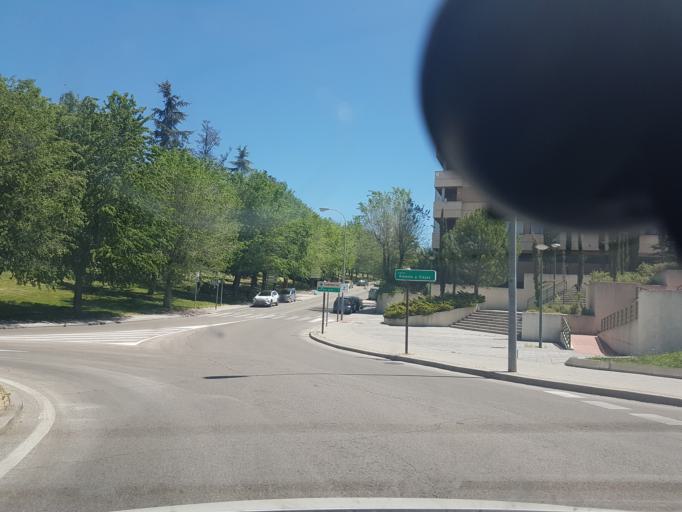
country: ES
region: Madrid
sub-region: Provincia de Madrid
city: Pozuelo de Alarcon
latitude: 40.4402
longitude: -3.8068
